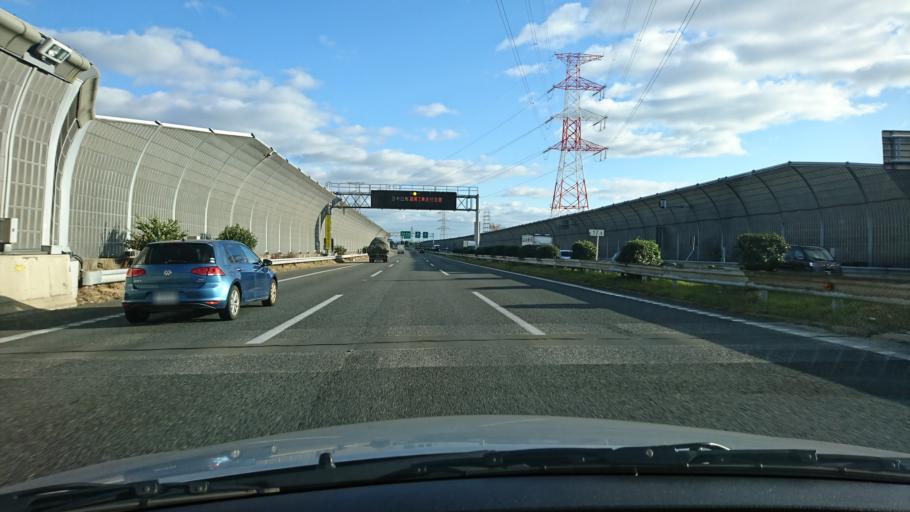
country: JP
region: Hyogo
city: Takarazuka
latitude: 34.8105
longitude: 135.3634
